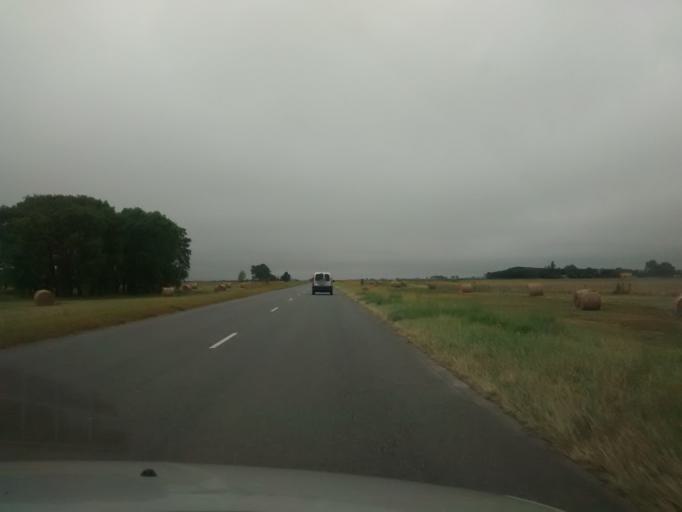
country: AR
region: Buenos Aires
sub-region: Partido de Ayacucho
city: Ayacucho
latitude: -37.2557
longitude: -58.4844
